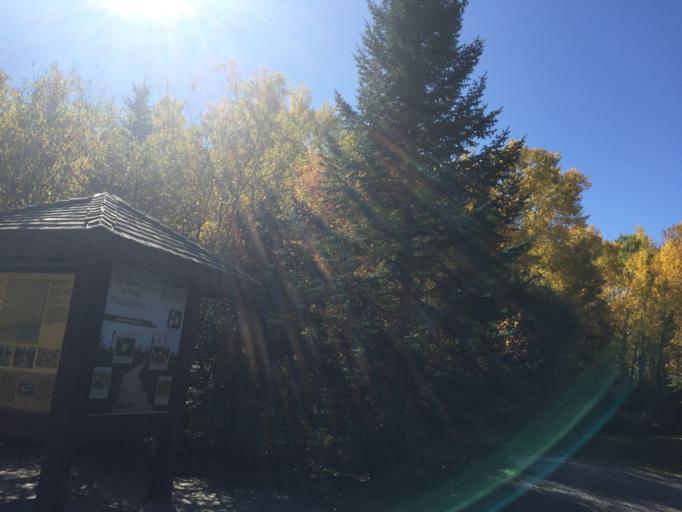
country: US
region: Minnesota
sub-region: Lake of the Woods County
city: Baudette
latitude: 48.2859
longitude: -94.5660
